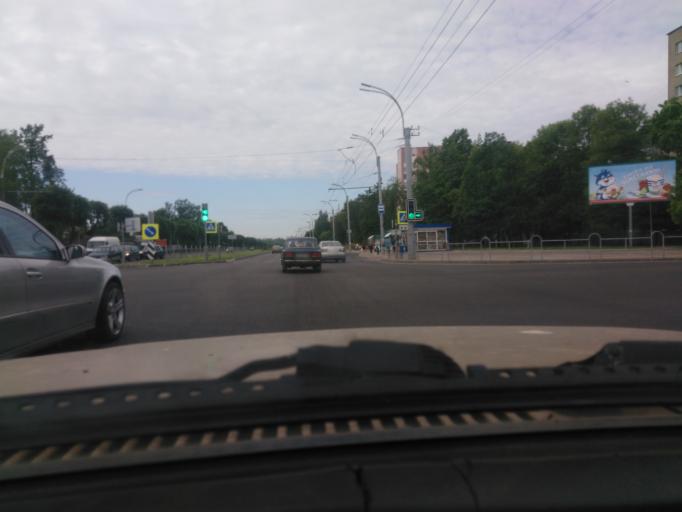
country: BY
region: Mogilev
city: Mahilyow
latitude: 53.9088
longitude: 30.3118
